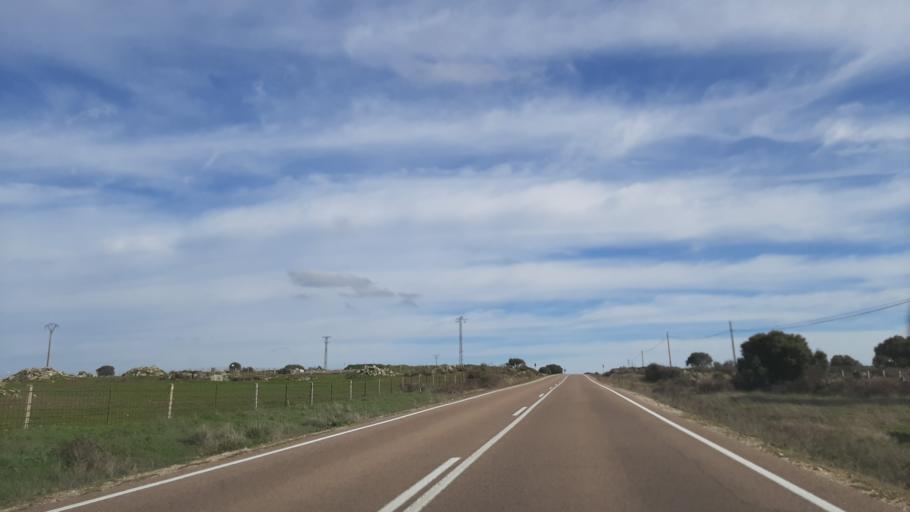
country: ES
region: Castille and Leon
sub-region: Provincia de Salamanca
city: Villaseco de los Reyes
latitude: 41.1618
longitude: -6.1790
